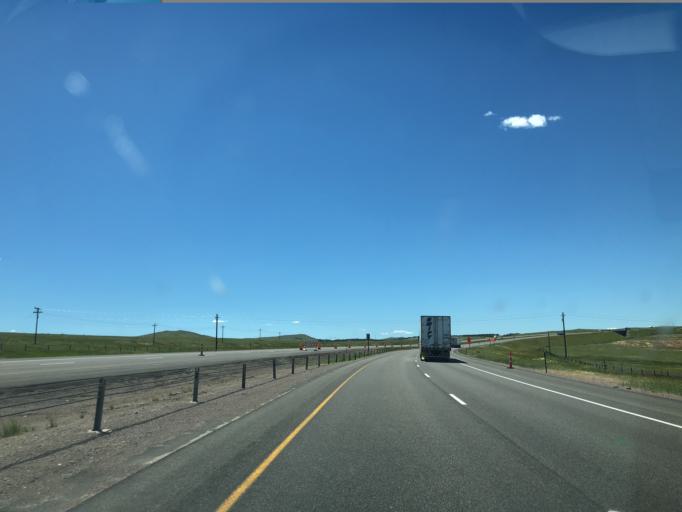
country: US
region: Wyoming
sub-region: Laramie County
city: Cheyenne
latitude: 41.0954
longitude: -105.1973
